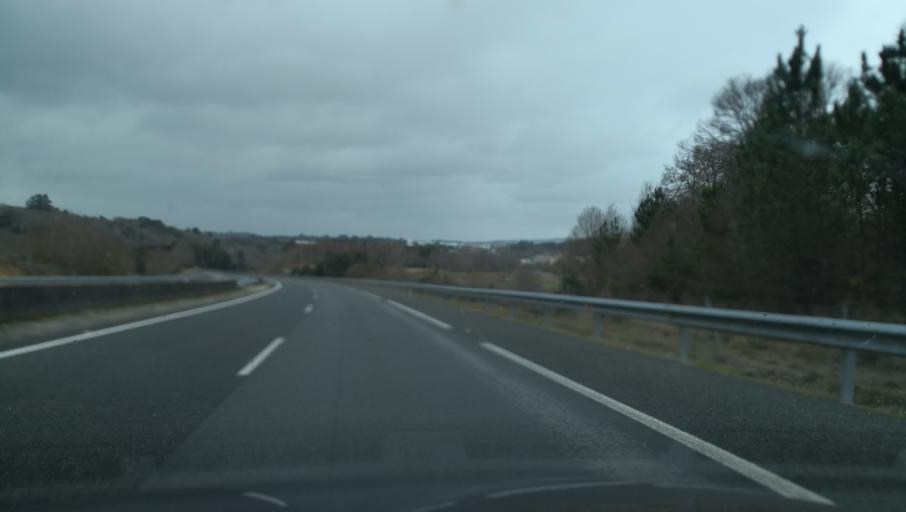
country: ES
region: Galicia
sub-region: Provincia de Pontevedra
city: Lalin
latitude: 42.6591
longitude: -8.1415
